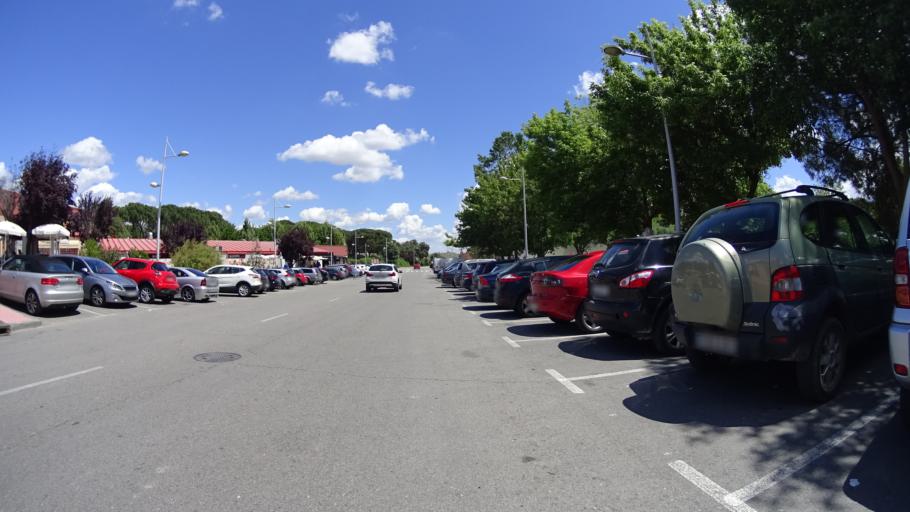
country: ES
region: Madrid
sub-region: Provincia de Madrid
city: Villanueva del Pardillo
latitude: 40.4652
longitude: -3.9490
